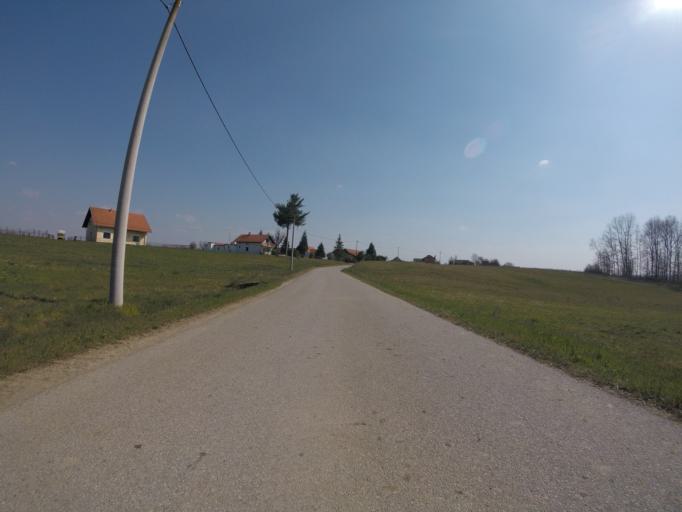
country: HR
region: Sisacko-Moslavacka
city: Gvozd
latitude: 45.5224
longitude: 15.9239
